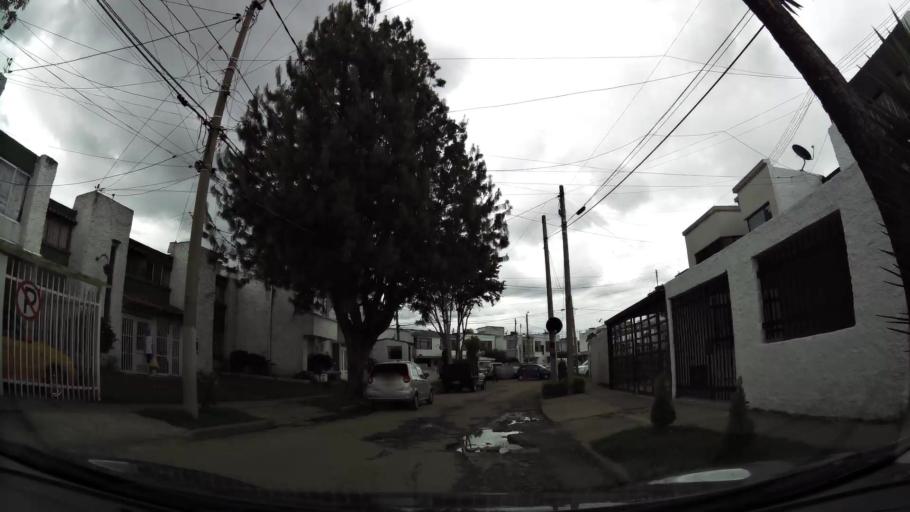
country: CO
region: Bogota D.C.
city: Barrio San Luis
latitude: 4.7058
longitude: -74.0915
